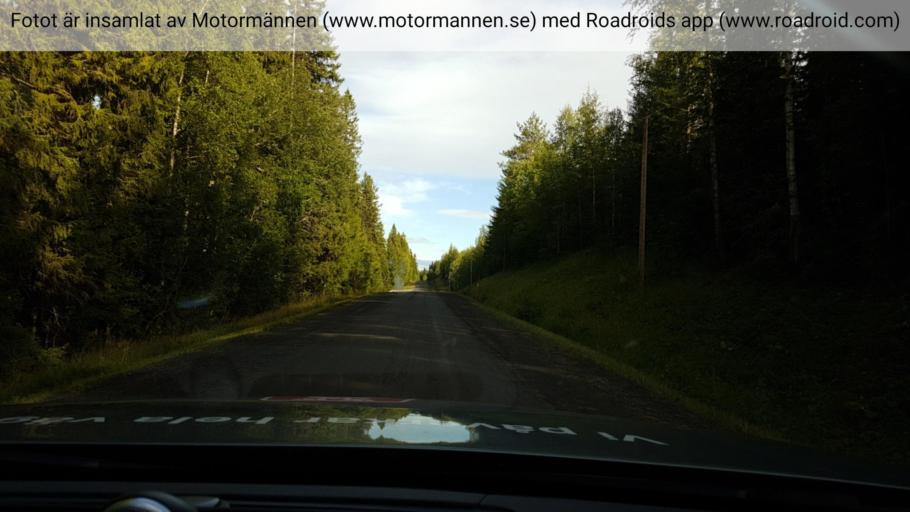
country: SE
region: Jaemtland
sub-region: Stroemsunds Kommun
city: Stroemsund
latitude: 64.1400
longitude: 15.7413
